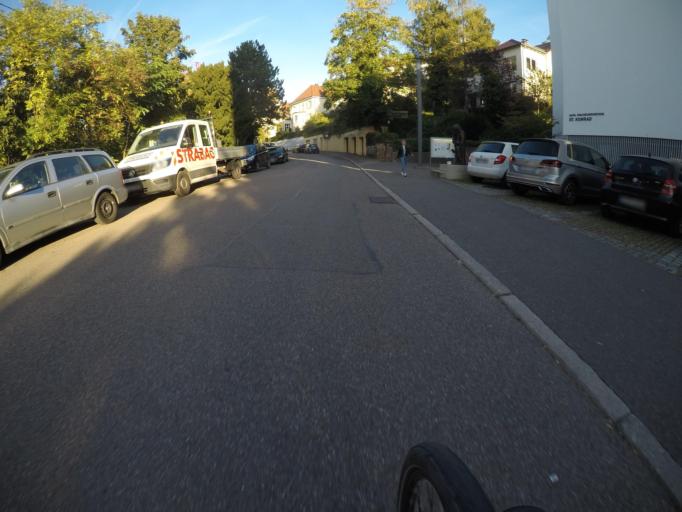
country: DE
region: Baden-Wuerttemberg
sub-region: Regierungsbezirk Stuttgart
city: Stuttgart
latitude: 48.7736
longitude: 9.1909
